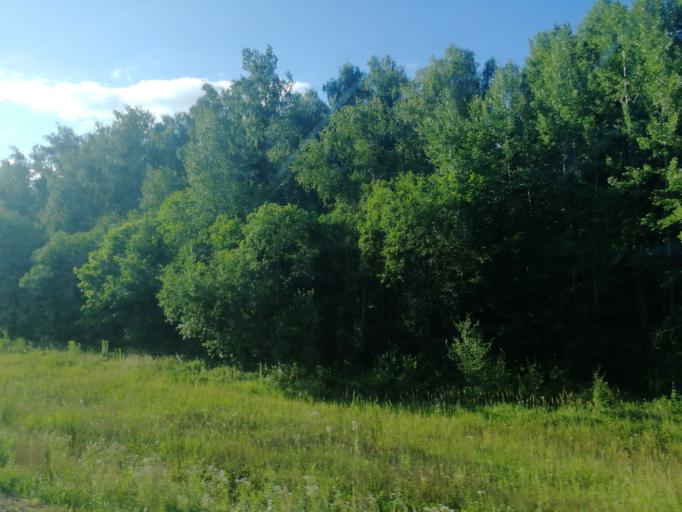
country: RU
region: Tula
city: Novogurovskiy
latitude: 54.2791
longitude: 37.2352
